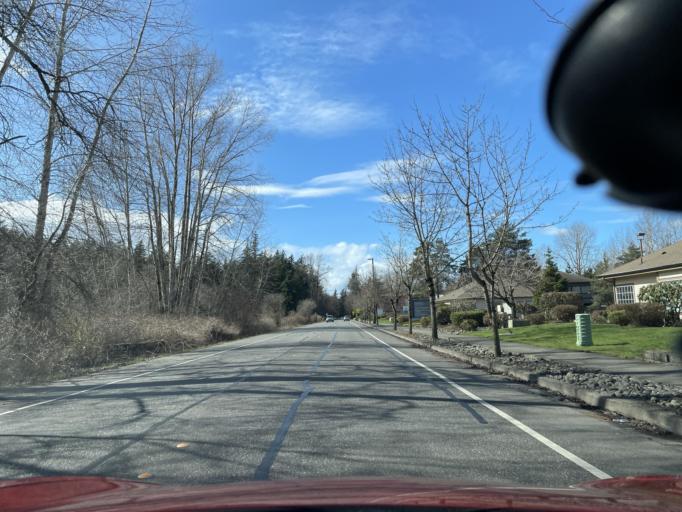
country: US
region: Washington
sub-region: Whatcom County
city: Bellingham
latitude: 48.7771
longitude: -122.4774
